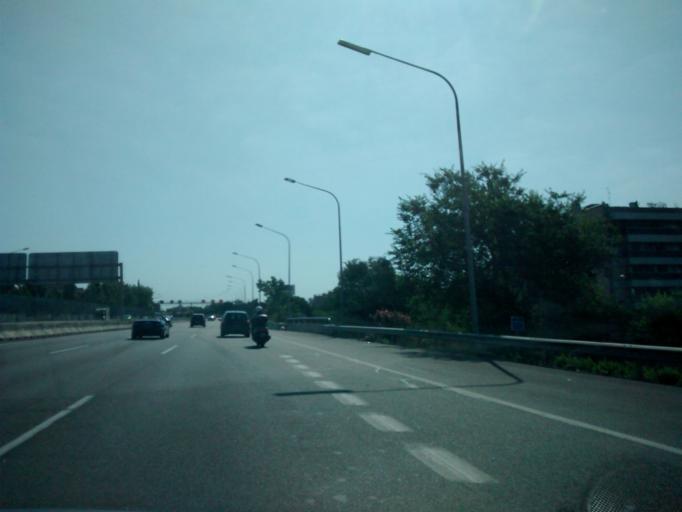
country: ES
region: Catalonia
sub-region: Provincia de Barcelona
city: Sant Just Desvern
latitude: 41.3763
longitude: 2.0765
